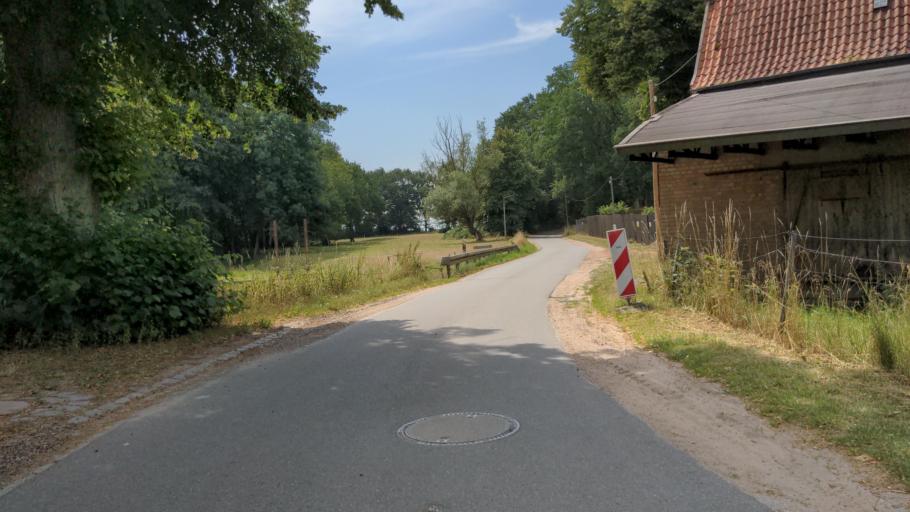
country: DE
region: Schleswig-Holstein
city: Gross Gronau
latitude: 53.8514
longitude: 10.7954
